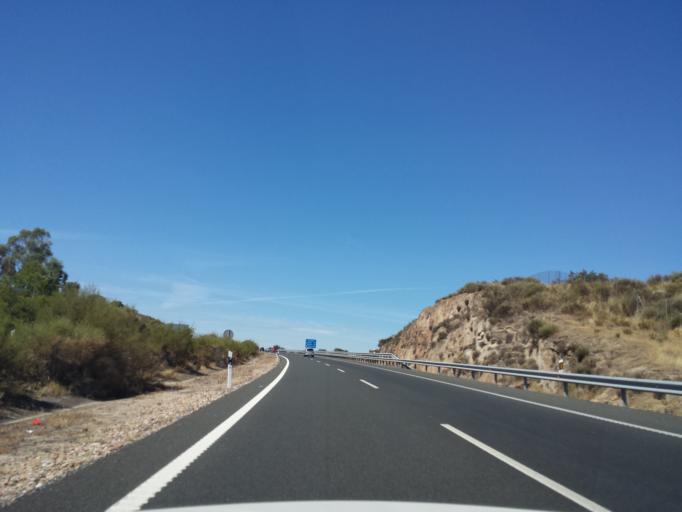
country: ES
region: Extremadura
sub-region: Provincia de Caceres
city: Navalmoral de la Mata
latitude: 39.8862
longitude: -5.5293
